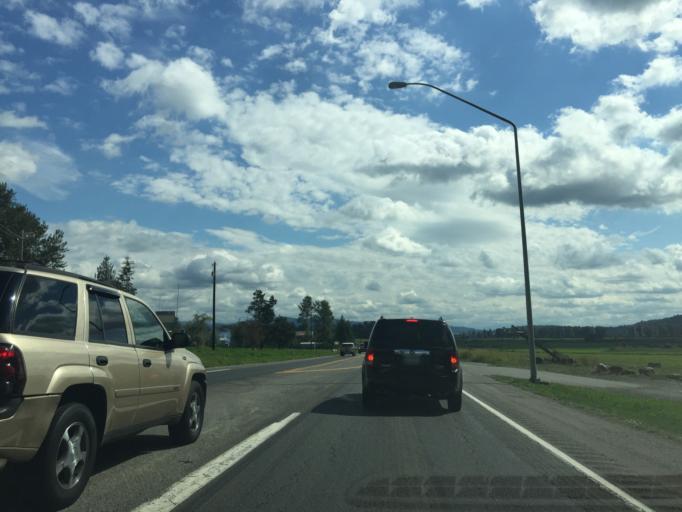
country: US
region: Washington
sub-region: Snohomish County
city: Three Lakes
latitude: 47.9008
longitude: -122.0368
